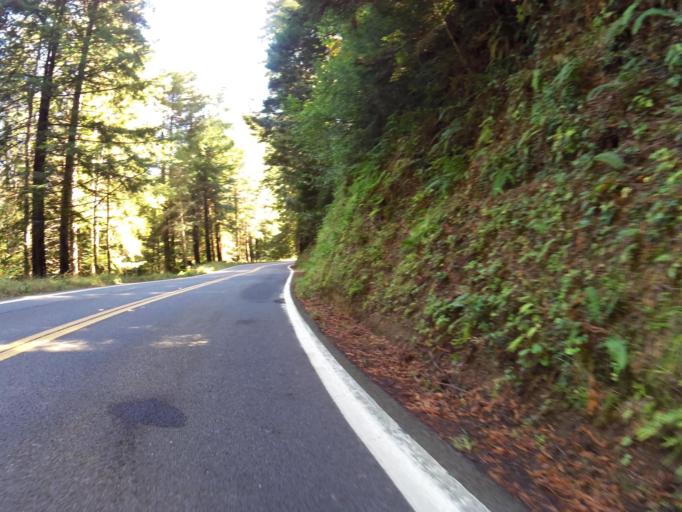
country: US
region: California
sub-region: Mendocino County
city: Fort Bragg
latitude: 39.7346
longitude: -123.8112
